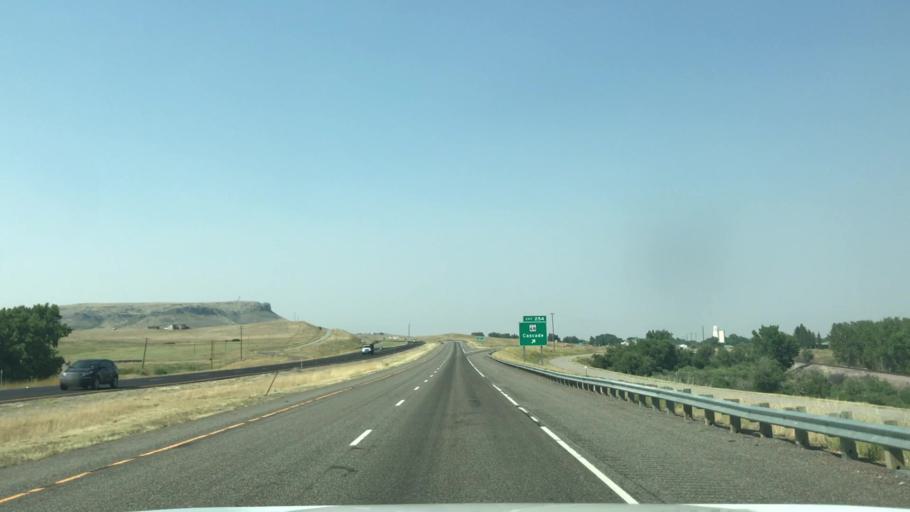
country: US
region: Montana
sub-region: Cascade County
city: Sun Prairie
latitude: 47.2552
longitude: -111.7093
